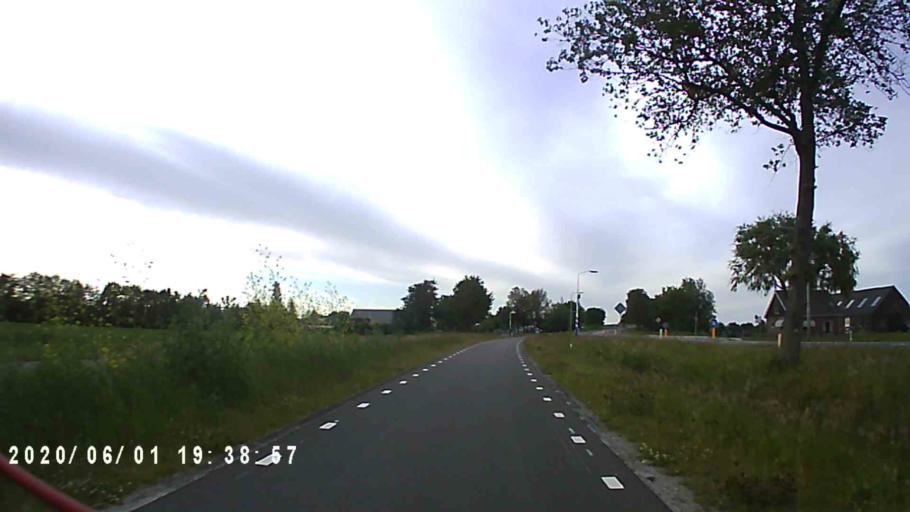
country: NL
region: Friesland
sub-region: Gemeente Achtkarspelen
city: Augustinusga
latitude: 53.2241
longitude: 6.1741
